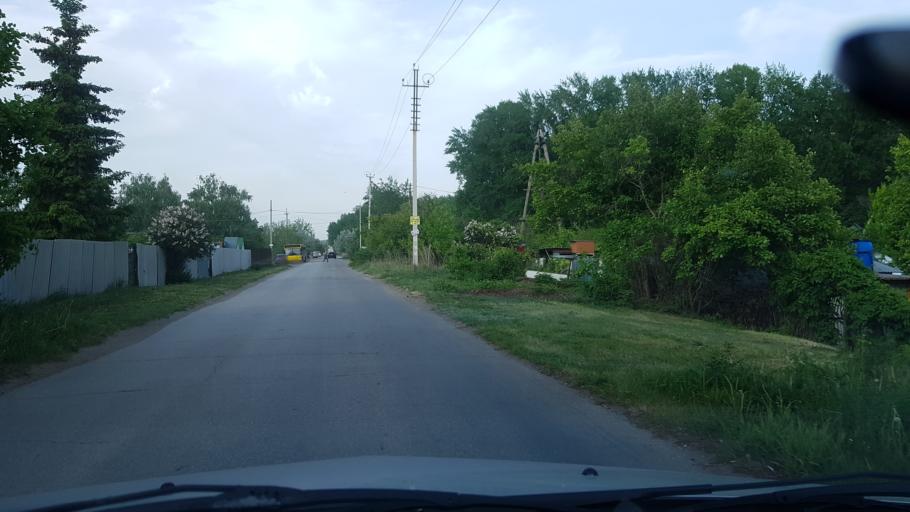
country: RU
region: Samara
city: Khryashchevka
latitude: 53.8250
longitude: 49.1695
